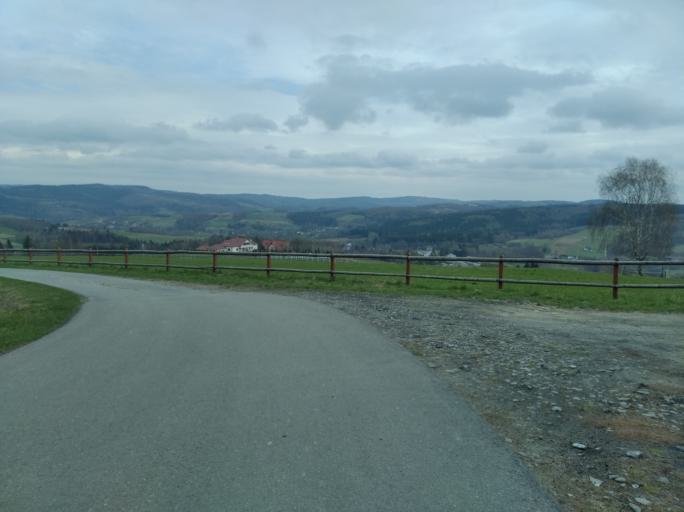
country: PL
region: Subcarpathian Voivodeship
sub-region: Powiat strzyzowski
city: Konieczkowa
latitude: 49.8220
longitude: 21.9111
